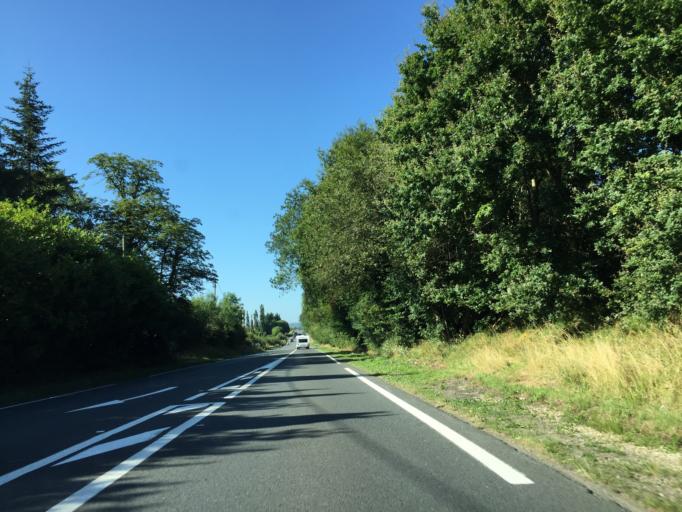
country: FR
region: Lower Normandy
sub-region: Departement du Calvados
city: Lisieux
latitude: 49.2414
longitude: 0.2220
